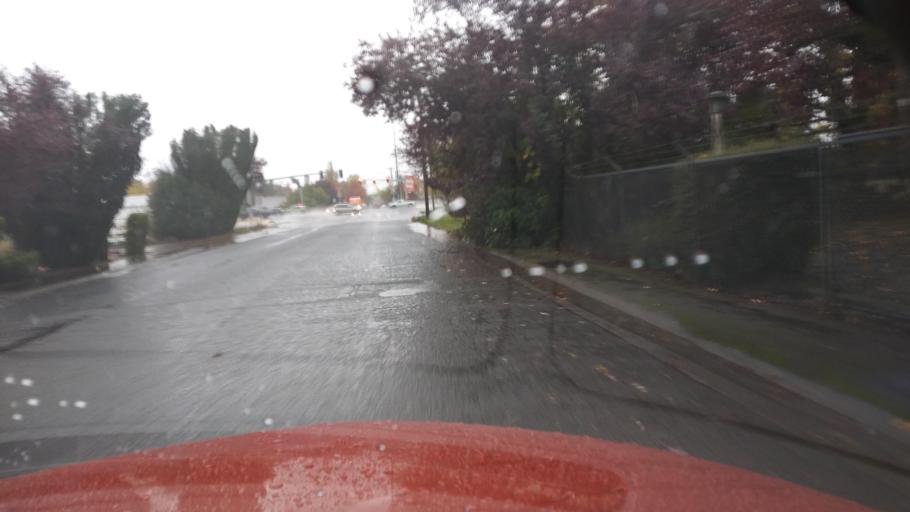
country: US
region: Oregon
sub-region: Washington County
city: Cornelius
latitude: 45.5212
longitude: -123.0399
